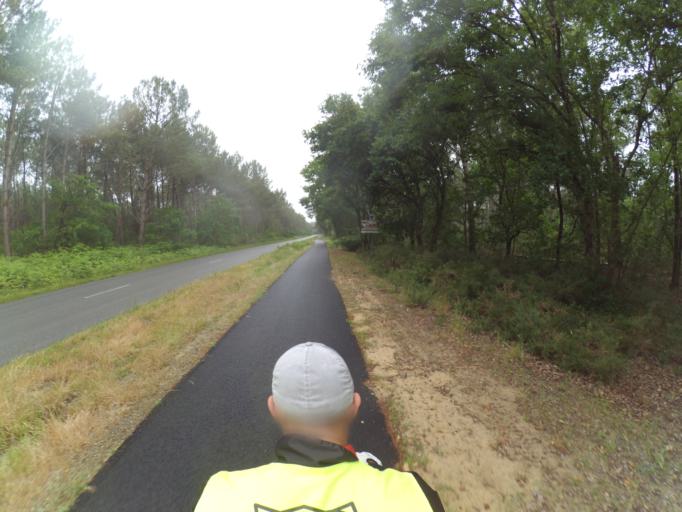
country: FR
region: Aquitaine
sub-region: Departement des Landes
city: Mimizan
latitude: 44.2369
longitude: -1.2164
